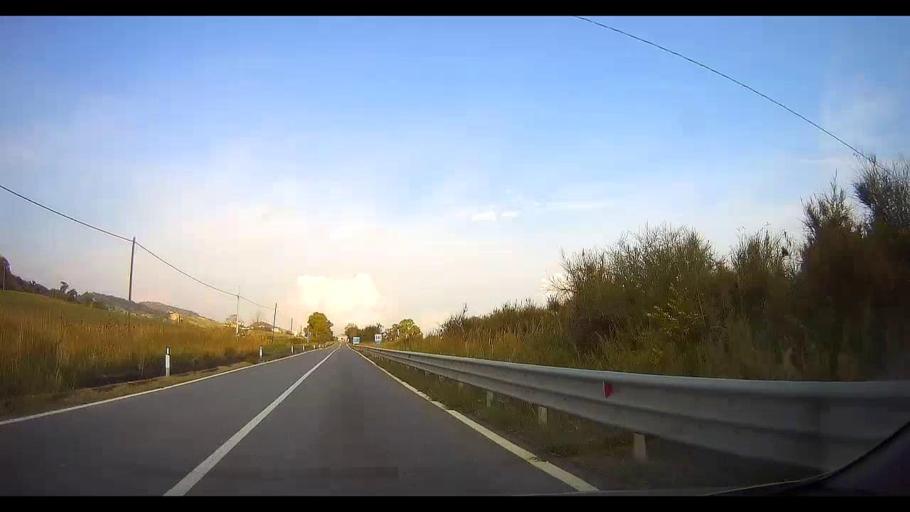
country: IT
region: Calabria
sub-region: Provincia di Cosenza
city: Cariati
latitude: 39.5201
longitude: 16.9041
